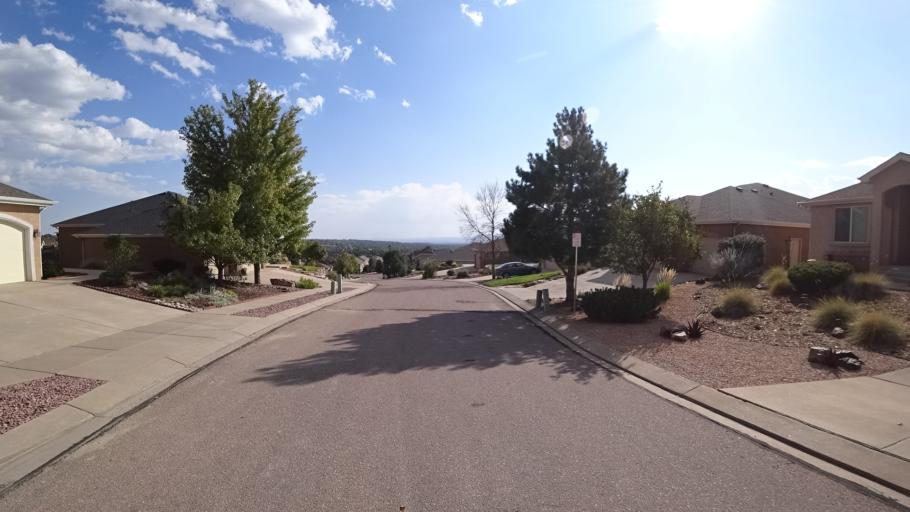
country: US
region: Colorado
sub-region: El Paso County
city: Cimarron Hills
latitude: 38.9124
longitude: -104.7381
